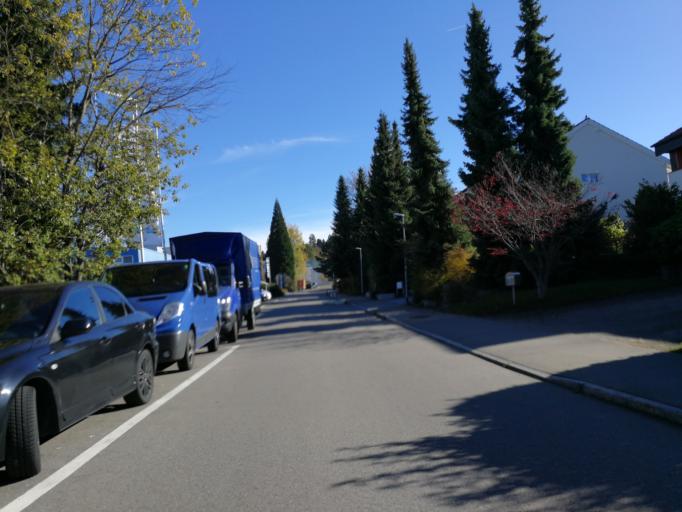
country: CH
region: Zurich
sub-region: Bezirk Meilen
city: Oetwil am See
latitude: 47.2742
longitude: 8.7246
